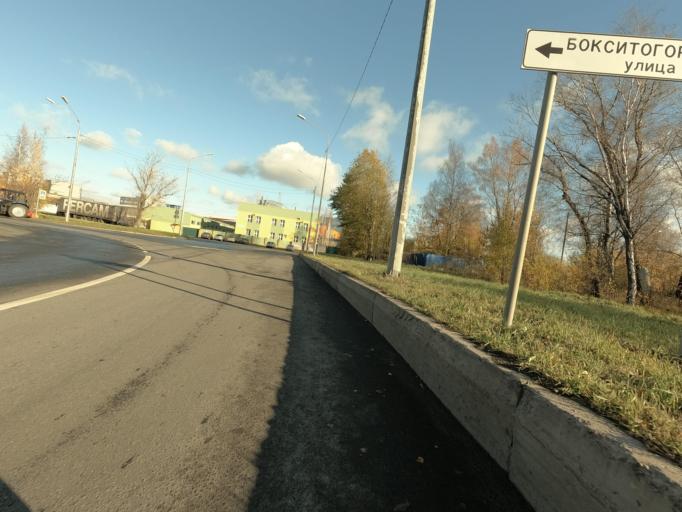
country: RU
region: St.-Petersburg
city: Krasnogvargeisky
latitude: 59.9483
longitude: 30.4476
